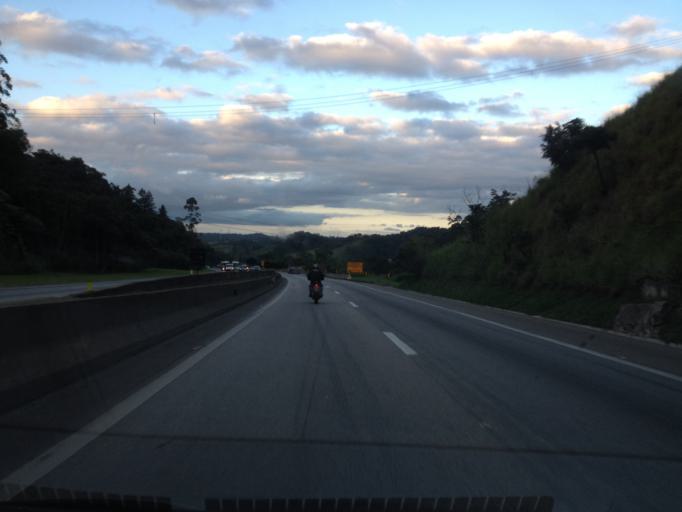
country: BR
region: Sao Paulo
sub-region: Aruja
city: Aruja
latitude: -23.4004
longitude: -46.3039
